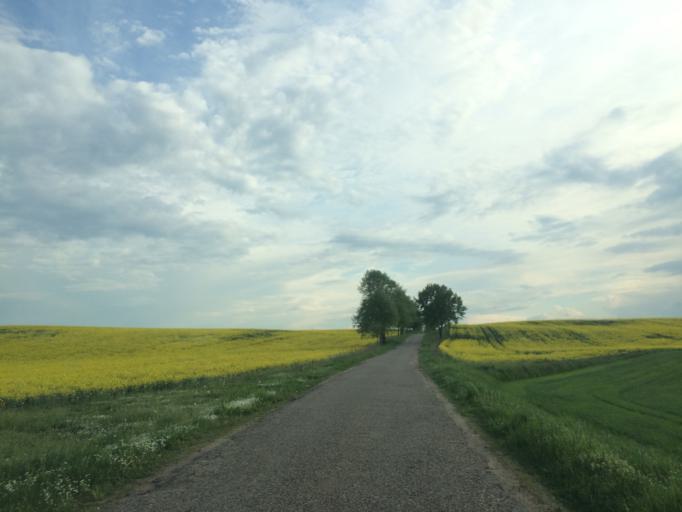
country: PL
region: Kujawsko-Pomorskie
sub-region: Powiat brodnicki
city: Brzozie
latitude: 53.3470
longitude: 19.5809
